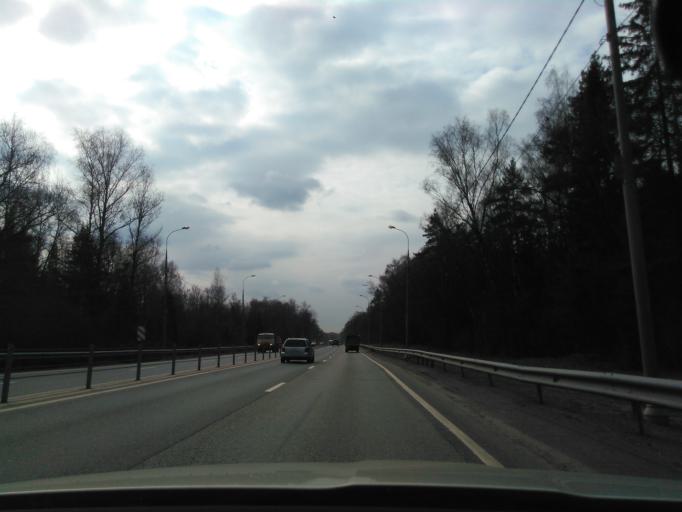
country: RU
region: Moskovskaya
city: Marfino
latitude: 56.0278
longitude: 37.5428
